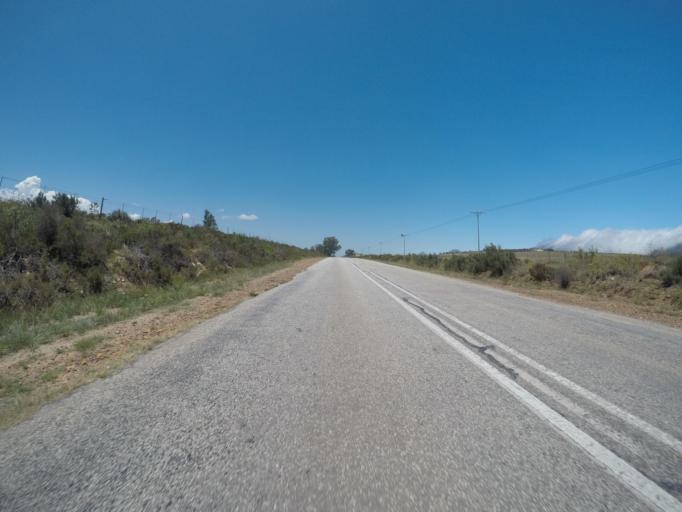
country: ZA
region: Western Cape
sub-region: Eden District Municipality
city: Plettenberg Bay
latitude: -33.7705
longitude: 23.5721
